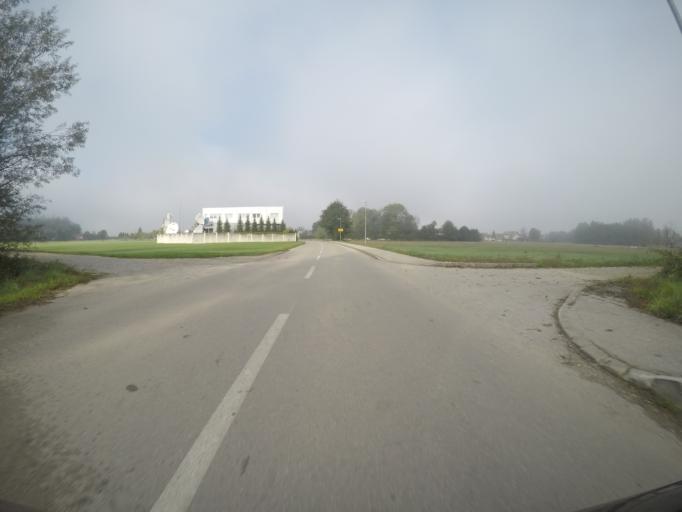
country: SI
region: Domzale
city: Dob
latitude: 46.1492
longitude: 14.6355
